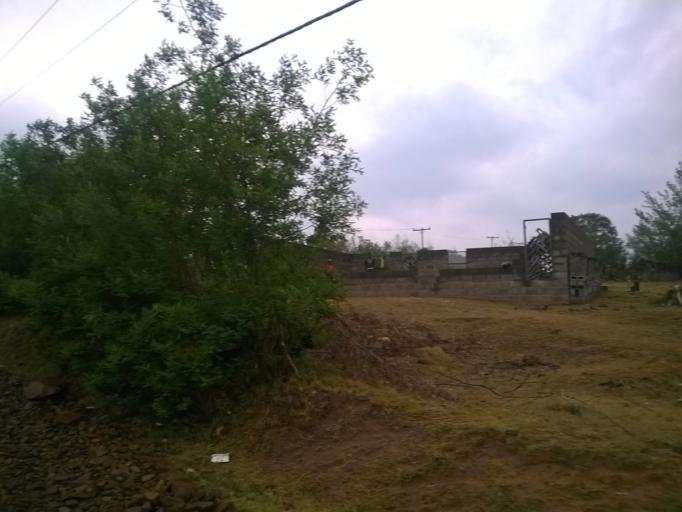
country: LS
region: Berea
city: Teyateyaneng
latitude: -29.1377
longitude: 27.7374
